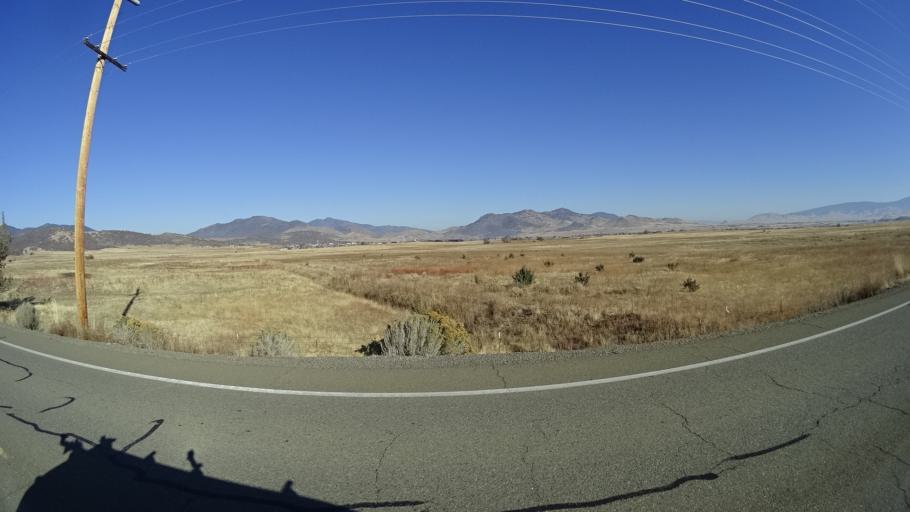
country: US
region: California
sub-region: Siskiyou County
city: Yreka
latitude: 41.7112
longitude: -122.5889
